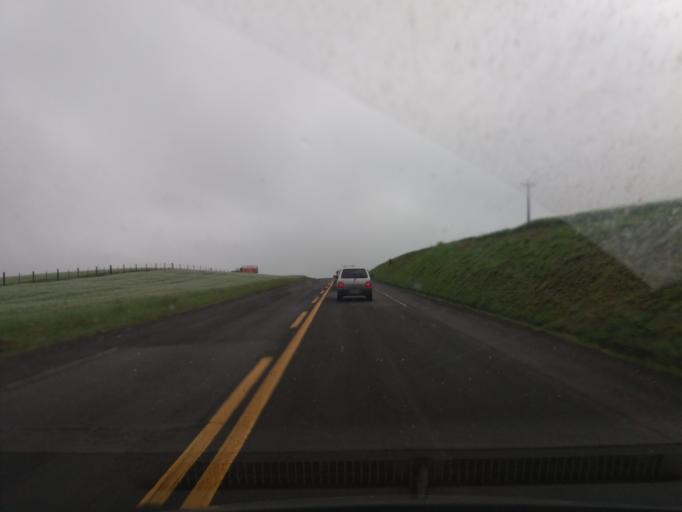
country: BR
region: Parana
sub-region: Realeza
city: Realeza
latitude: -25.8226
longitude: -53.5195
